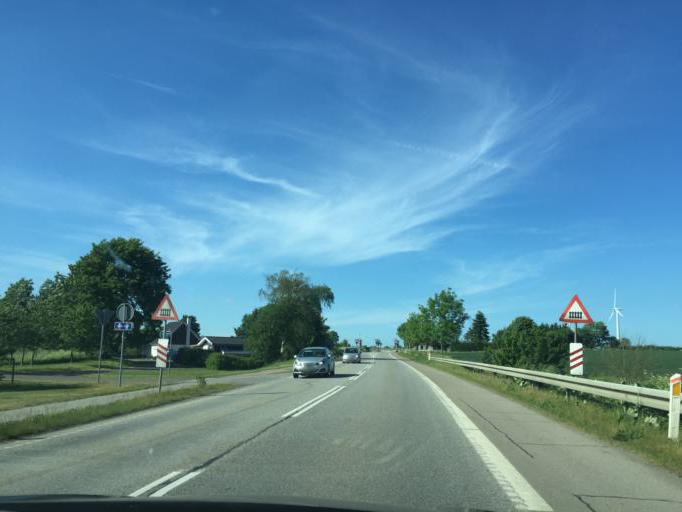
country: DK
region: Zealand
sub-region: Stevns Kommune
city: Harlev
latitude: 55.3532
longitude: 12.2488
